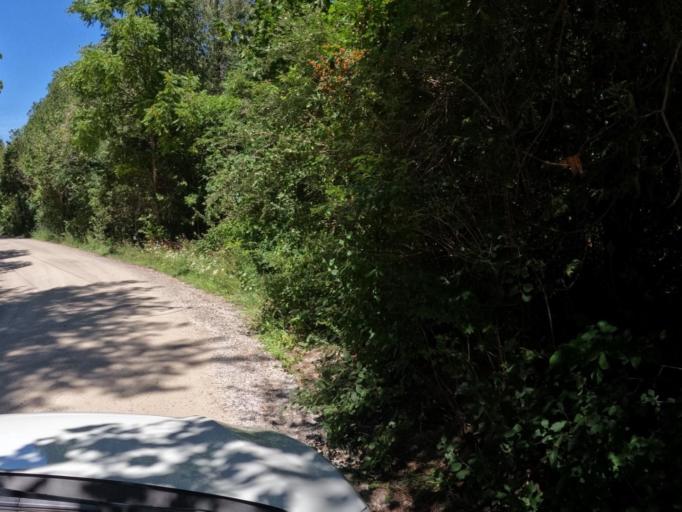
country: CA
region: Ontario
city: Cambridge
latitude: 43.4107
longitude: -80.2616
